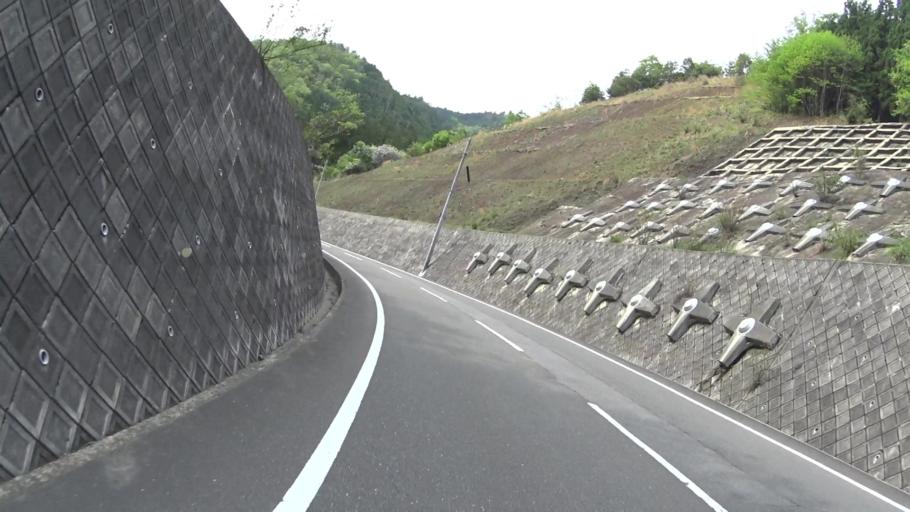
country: JP
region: Kyoto
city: Kameoka
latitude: 35.1480
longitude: 135.6216
